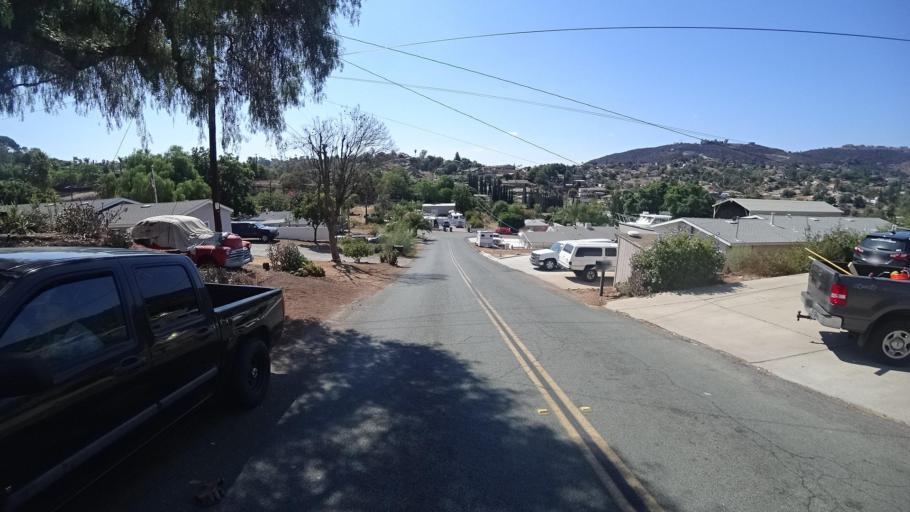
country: US
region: California
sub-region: San Diego County
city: Winter Gardens
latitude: 32.8405
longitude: -116.9302
